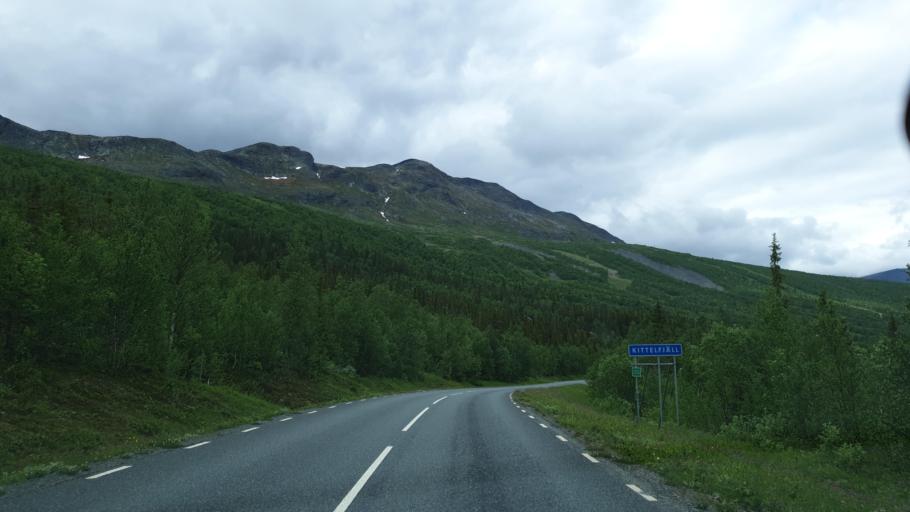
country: SE
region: Vaesterbotten
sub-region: Vilhelmina Kommun
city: Sjoberg
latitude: 65.2436
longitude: 15.4741
